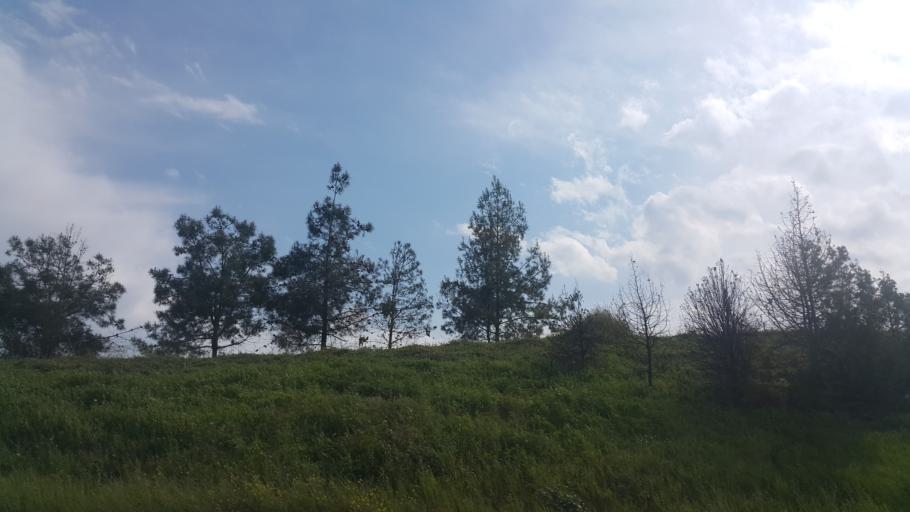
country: TR
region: Mersin
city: Tarsus
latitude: 36.9519
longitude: 34.7709
